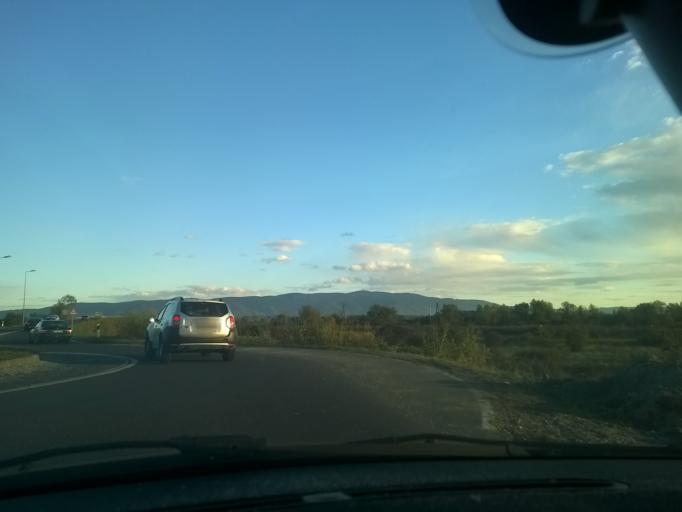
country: HR
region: Krapinsko-Zagorska
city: Zabok
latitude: 46.0138
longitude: 15.8710
